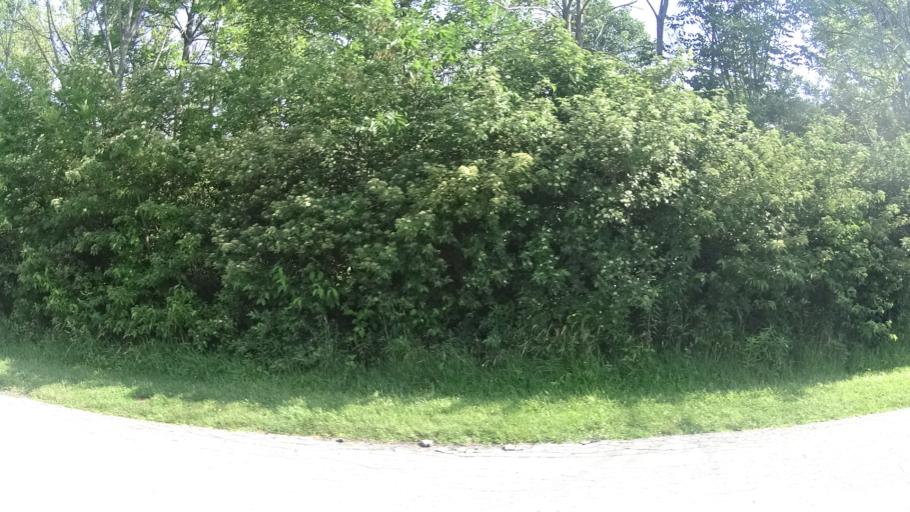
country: US
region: Ohio
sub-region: Erie County
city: Huron
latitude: 41.3779
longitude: -82.5082
